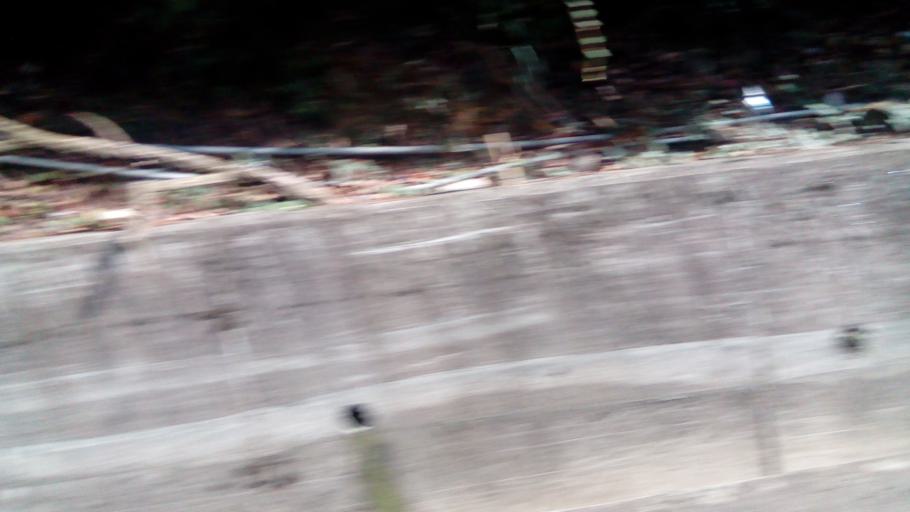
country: TW
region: Taiwan
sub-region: Hualien
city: Hualian
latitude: 24.3245
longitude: 121.3048
